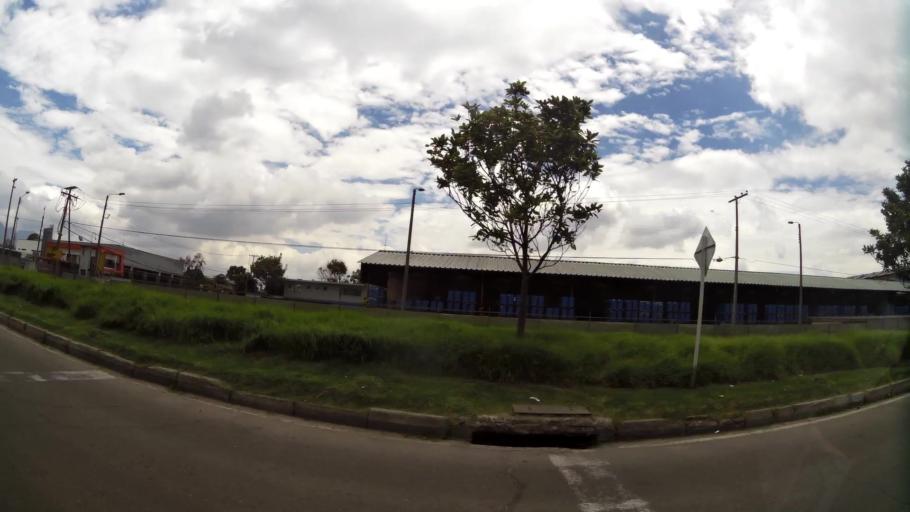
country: CO
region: Bogota D.C.
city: Bogota
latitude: 4.6386
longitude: -74.1038
